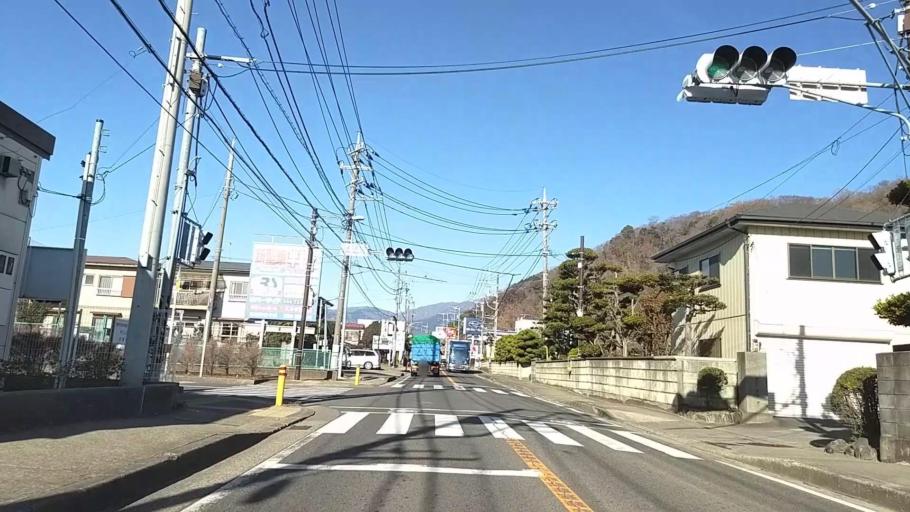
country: JP
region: Kanagawa
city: Hadano
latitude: 35.3662
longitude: 139.2424
